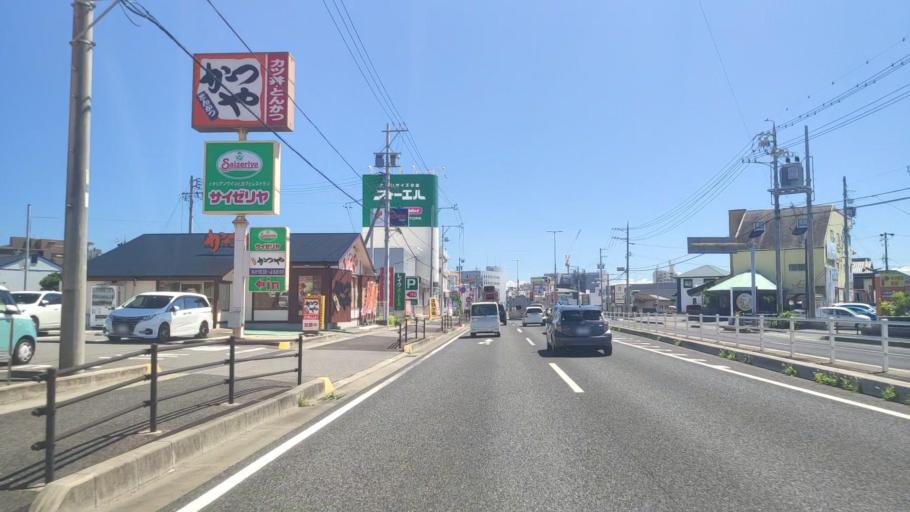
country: JP
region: Mie
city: Suzuka
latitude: 34.8403
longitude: 136.5885
